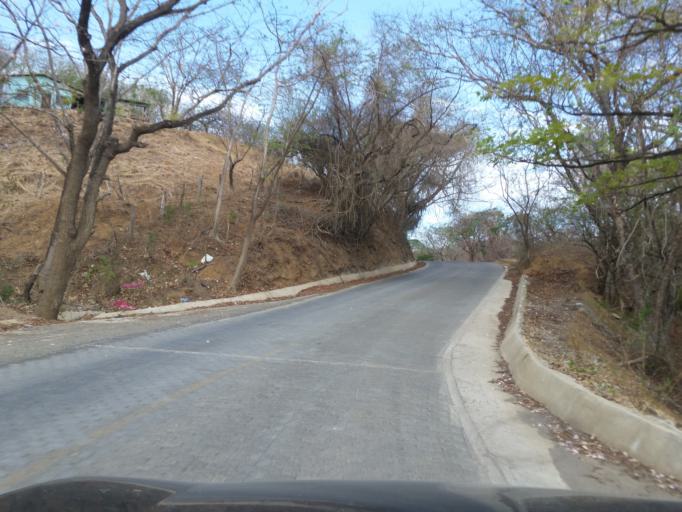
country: NI
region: Rivas
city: Tola
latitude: 11.3918
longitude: -85.9794
